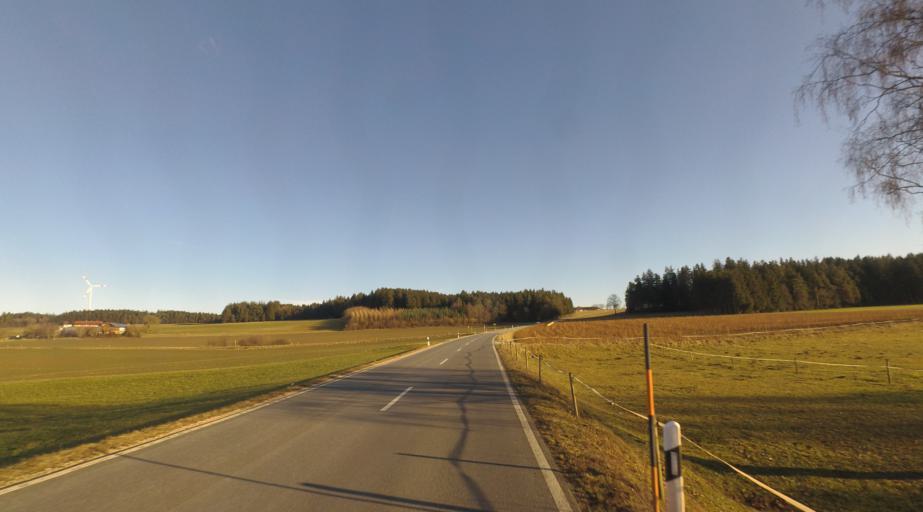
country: DE
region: Bavaria
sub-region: Upper Bavaria
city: Palling
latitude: 48.0140
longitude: 12.6130
